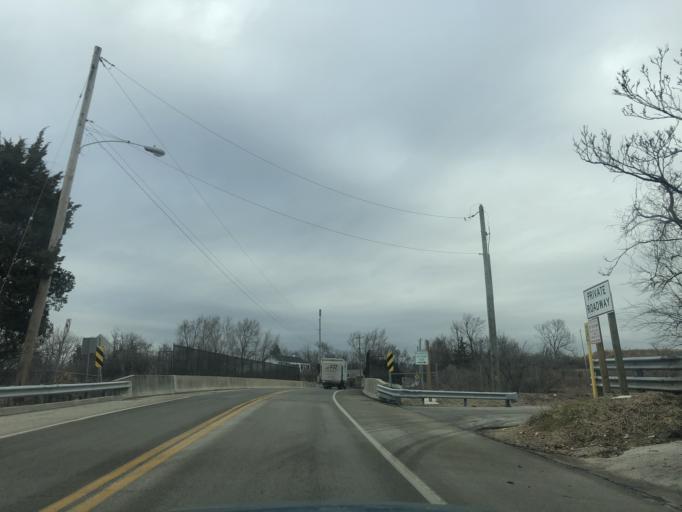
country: US
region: Pennsylvania
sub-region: Montgomery County
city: Conshohocken
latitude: 40.1055
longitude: -75.3122
